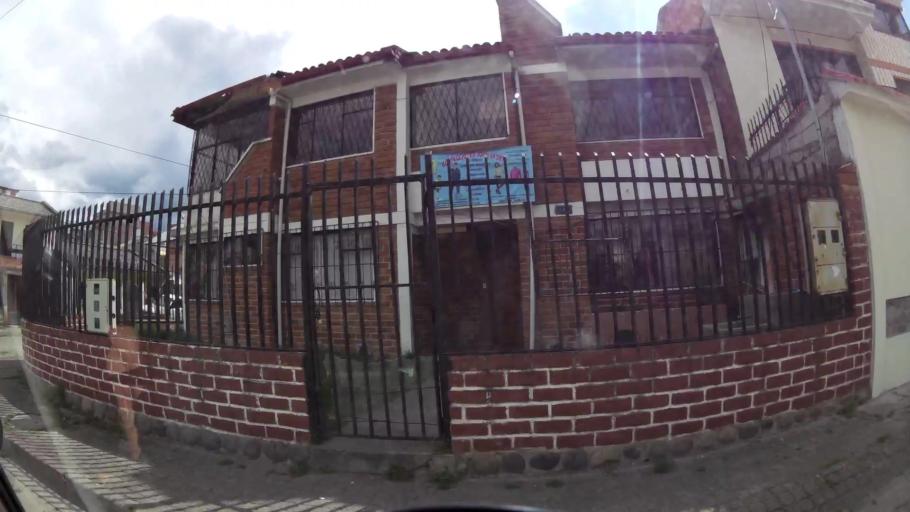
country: EC
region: Azuay
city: Cuenca
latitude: -2.8827
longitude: -78.9812
